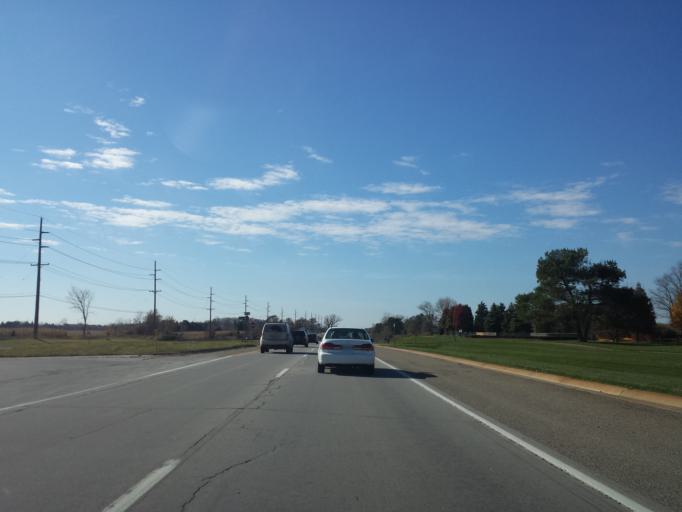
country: US
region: Michigan
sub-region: Oakland County
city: Milford
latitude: 42.6369
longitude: -83.6495
